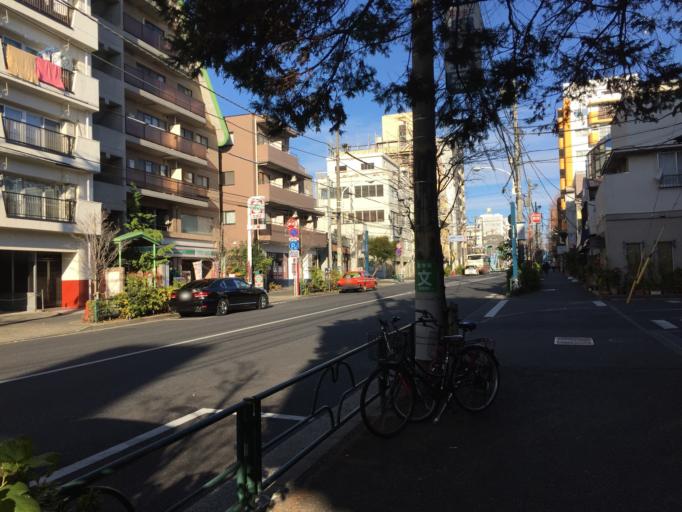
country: JP
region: Tokyo
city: Tokyo
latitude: 35.6440
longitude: 139.6798
